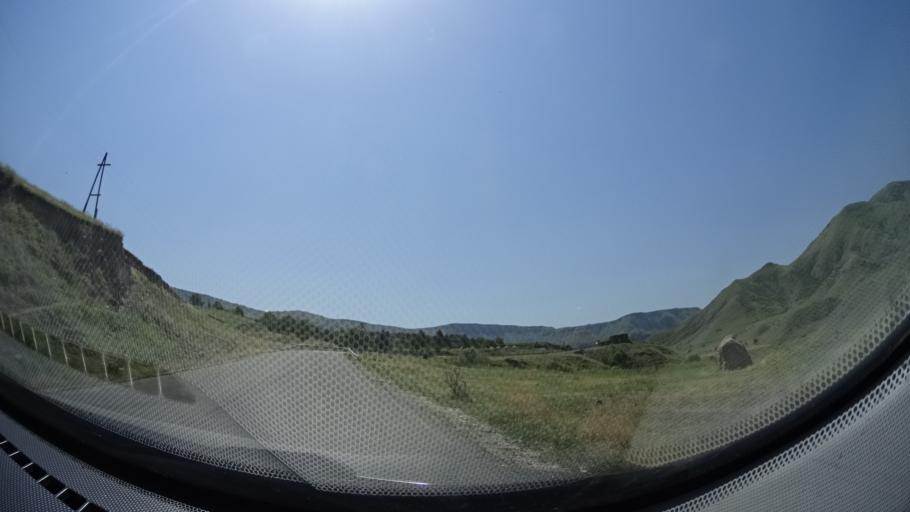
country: GE
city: Akhalk'alak'i
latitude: 41.4201
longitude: 43.3245
